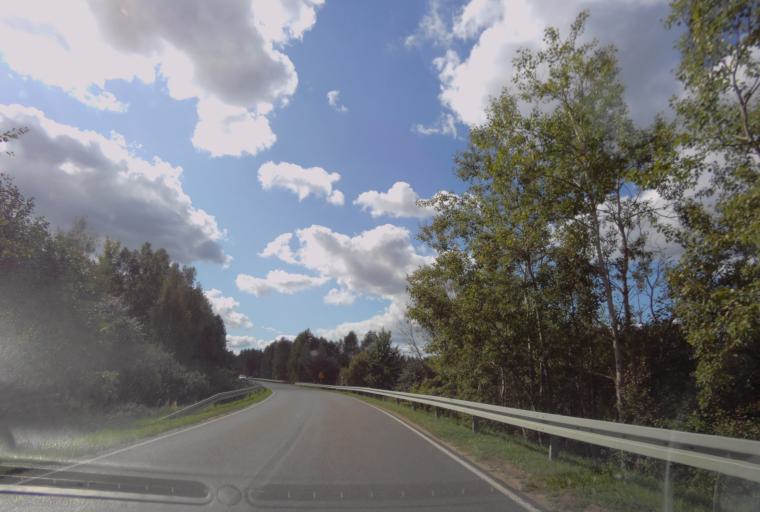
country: PL
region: Subcarpathian Voivodeship
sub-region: Powiat tarnobrzeski
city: Nowa Deba
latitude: 50.4077
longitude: 21.8130
